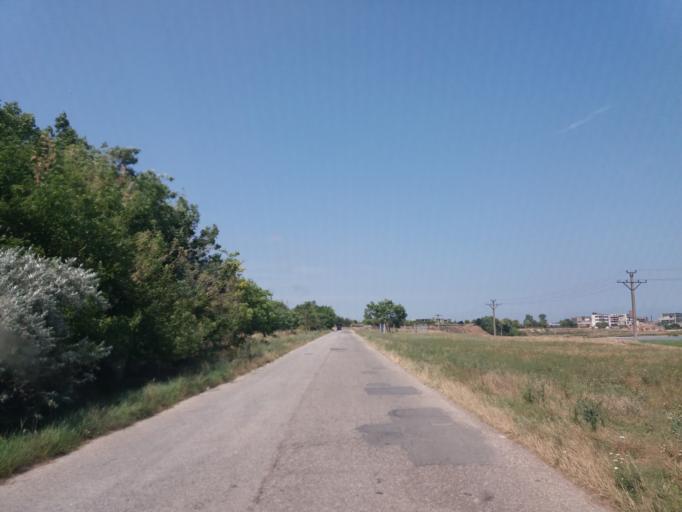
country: RO
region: Constanta
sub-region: Comuna Sacele
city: Sacele
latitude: 44.4435
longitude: 28.7313
